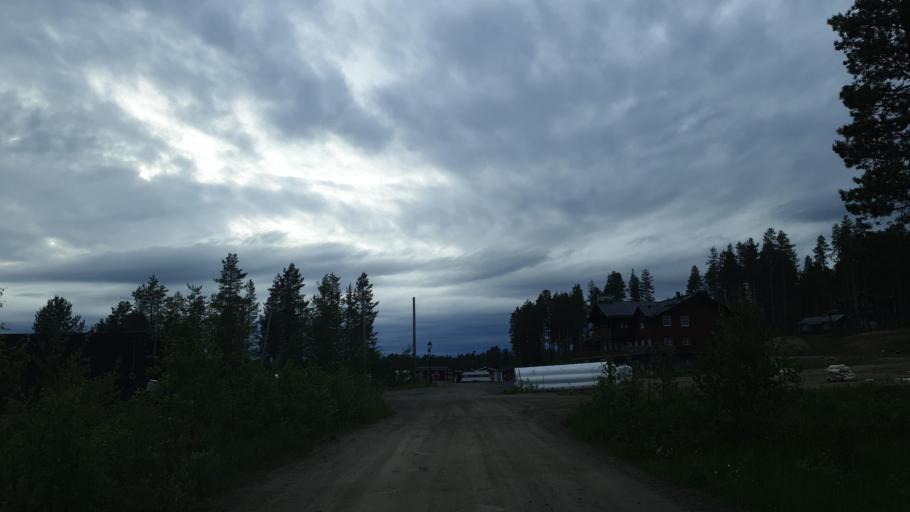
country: SE
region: Norrbotten
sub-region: Jokkmokks Kommun
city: Jokkmokk
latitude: 66.1542
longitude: 19.9905
